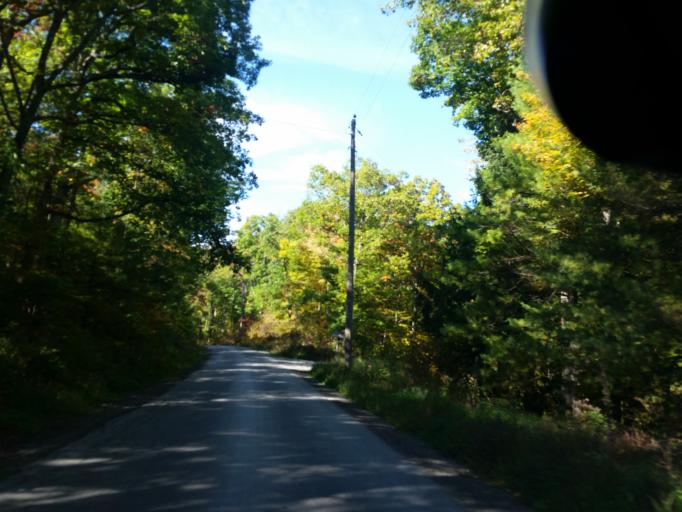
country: US
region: Pennsylvania
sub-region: Lycoming County
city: Duboistown
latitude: 41.1010
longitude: -77.1156
